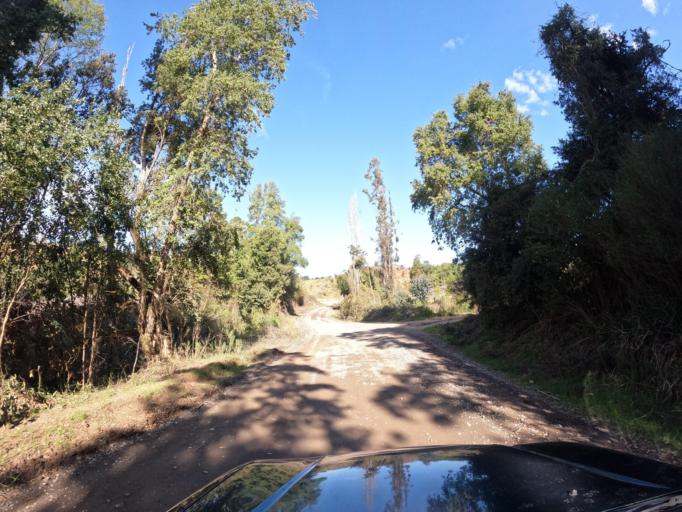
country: CL
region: Biobio
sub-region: Provincia de Biobio
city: La Laja
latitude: -37.0811
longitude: -72.8348
